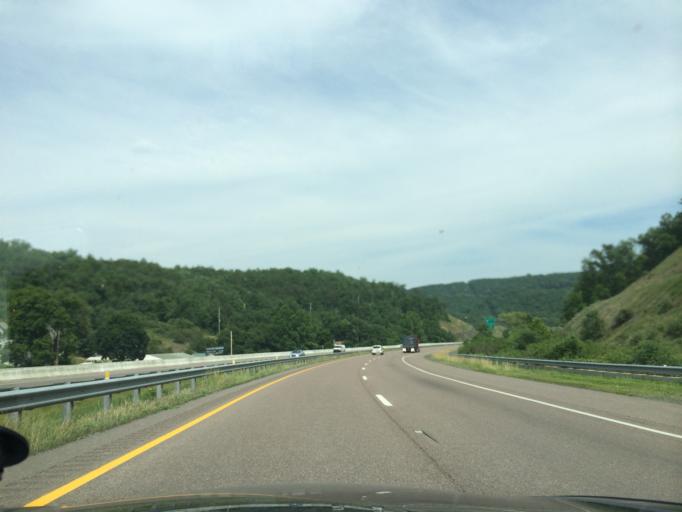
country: US
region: West Virginia
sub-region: Morgan County
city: Berkeley Springs
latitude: 39.6780
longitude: -78.4671
